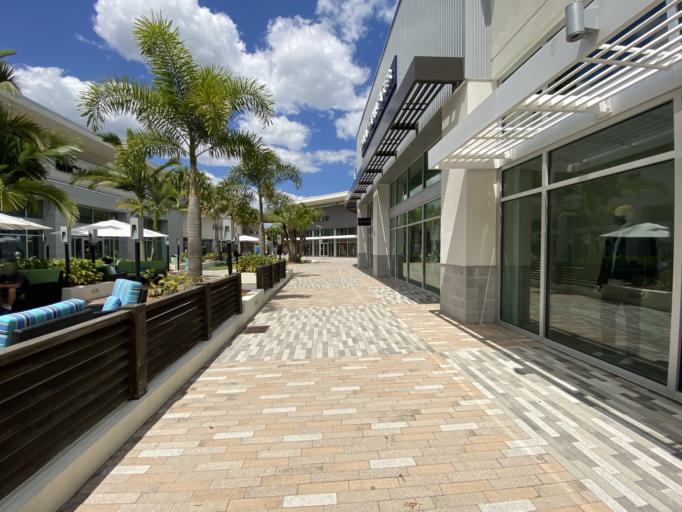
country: US
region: Florida
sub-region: Volusia County
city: Holly Hill
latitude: 29.2135
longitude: -81.0985
